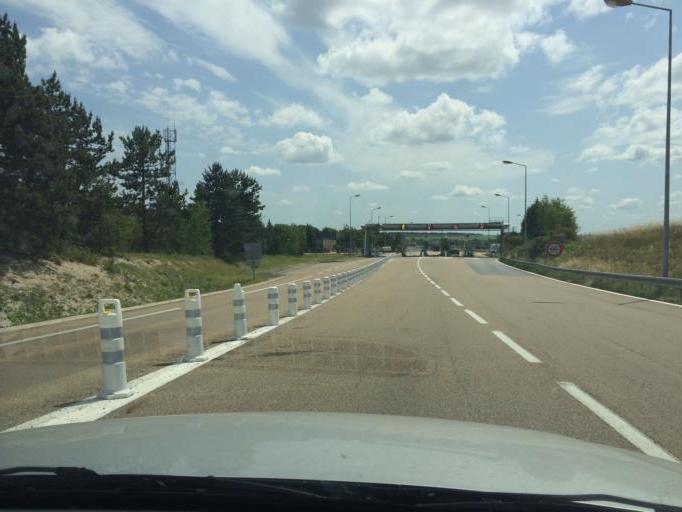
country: FR
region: Champagne-Ardenne
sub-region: Departement de la Marne
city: Fagnieres
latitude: 49.0421
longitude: 4.3209
